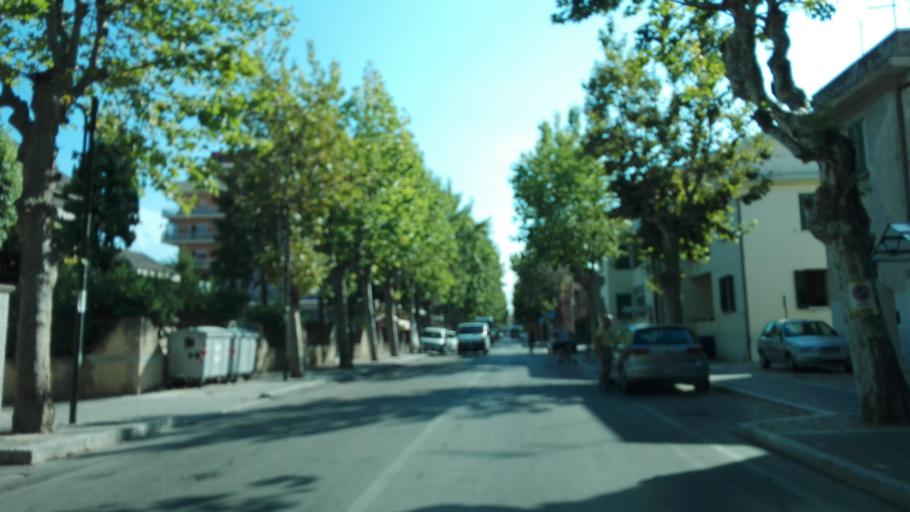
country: IT
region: Abruzzo
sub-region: Provincia di Pescara
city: Montesilvano Marina
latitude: 42.5158
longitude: 14.1595
